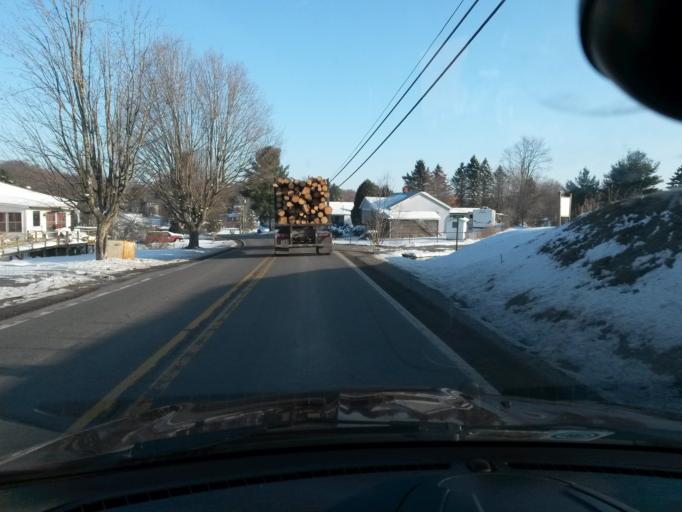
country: US
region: West Virginia
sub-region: Nicholas County
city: Craigsville
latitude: 38.2132
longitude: -80.6787
